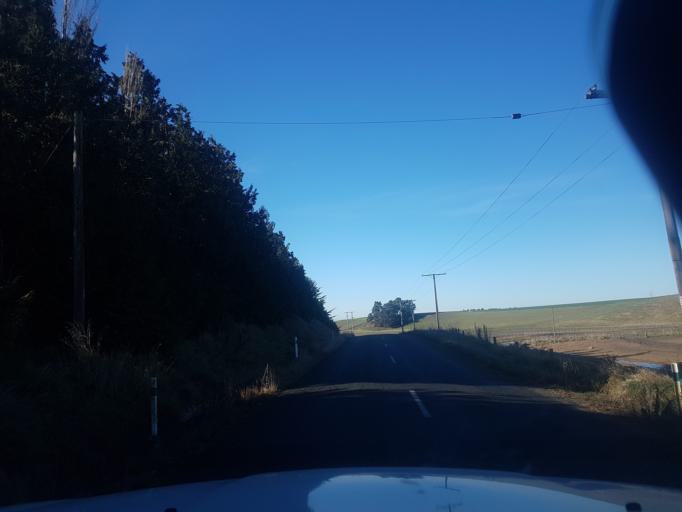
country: NZ
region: Canterbury
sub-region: Timaru District
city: Pleasant Point
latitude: -44.2723
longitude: 171.1291
